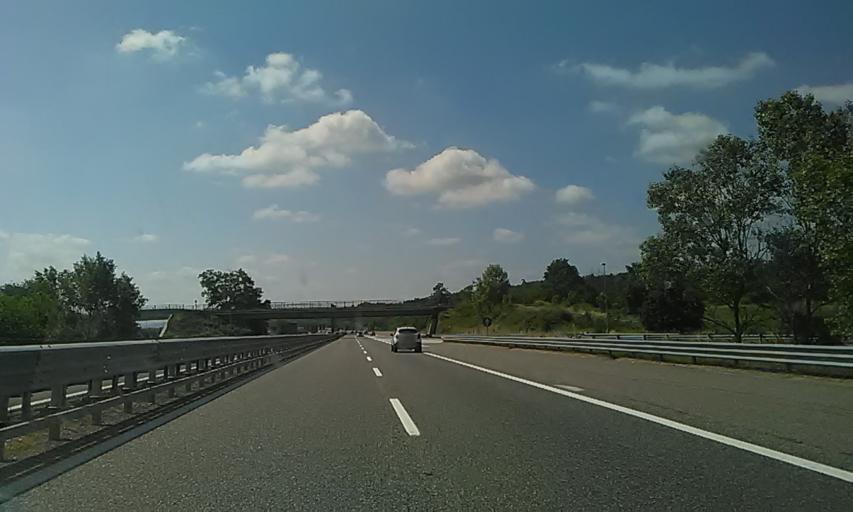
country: IT
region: Piedmont
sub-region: Provincia di Alessandria
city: Predosa
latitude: 44.7553
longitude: 8.6459
